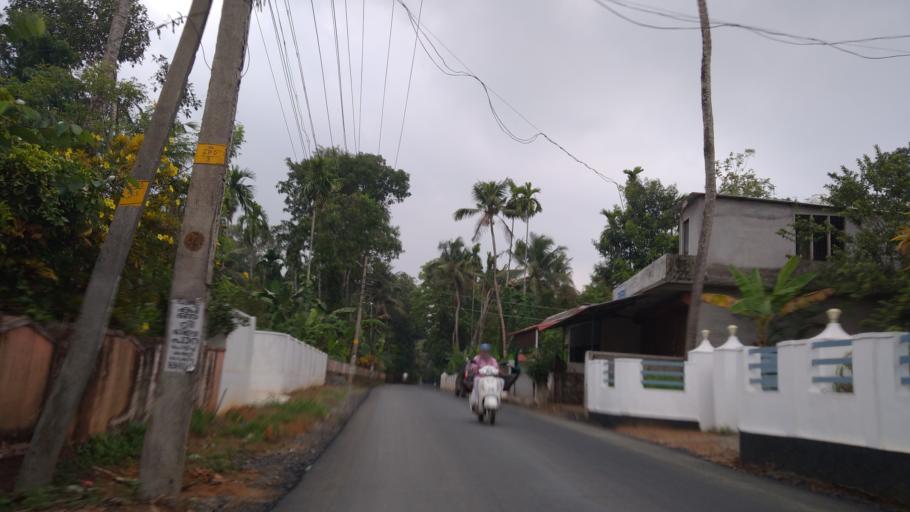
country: IN
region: Kerala
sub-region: Ernakulam
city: Perumbavoor
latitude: 10.0646
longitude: 76.5041
